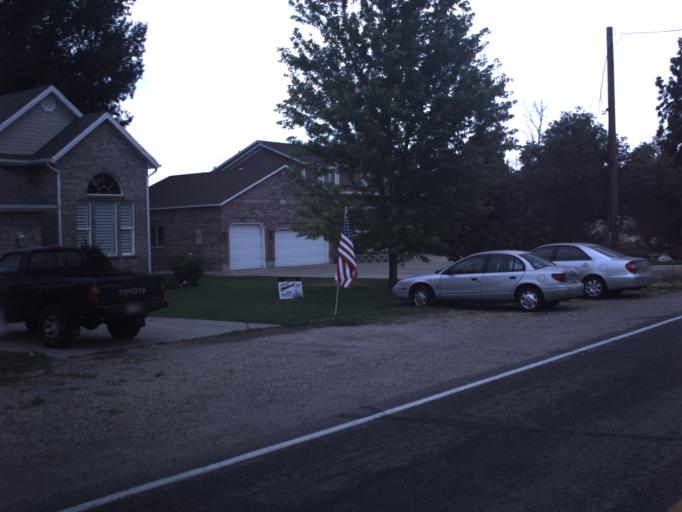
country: US
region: Utah
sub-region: Davis County
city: West Point
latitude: 41.0905
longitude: -112.1128
